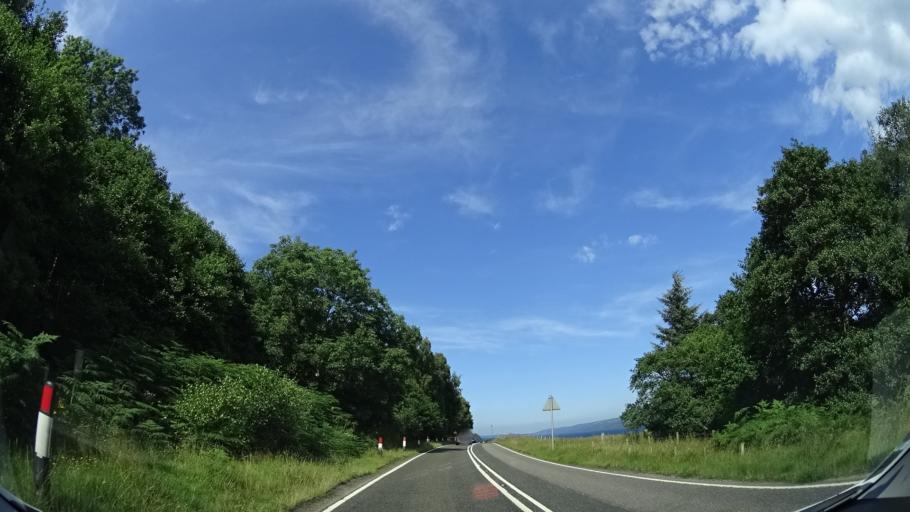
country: GB
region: Scotland
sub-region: Highland
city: Beauly
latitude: 57.3004
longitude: -4.4711
